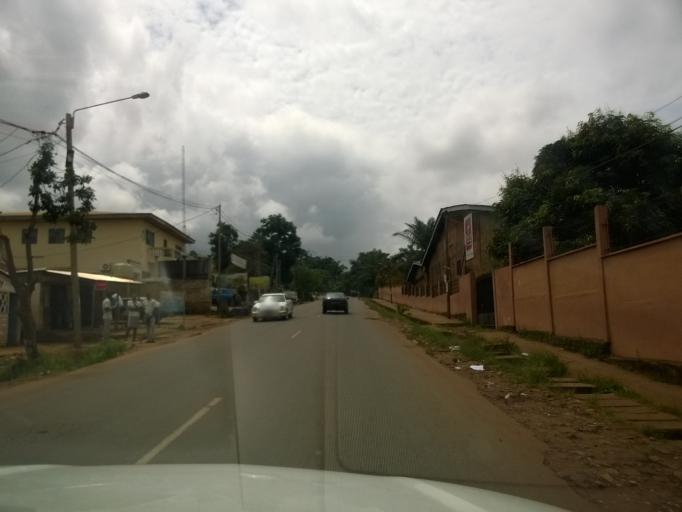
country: CM
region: Centre
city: Yaounde
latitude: 3.8418
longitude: 11.5000
